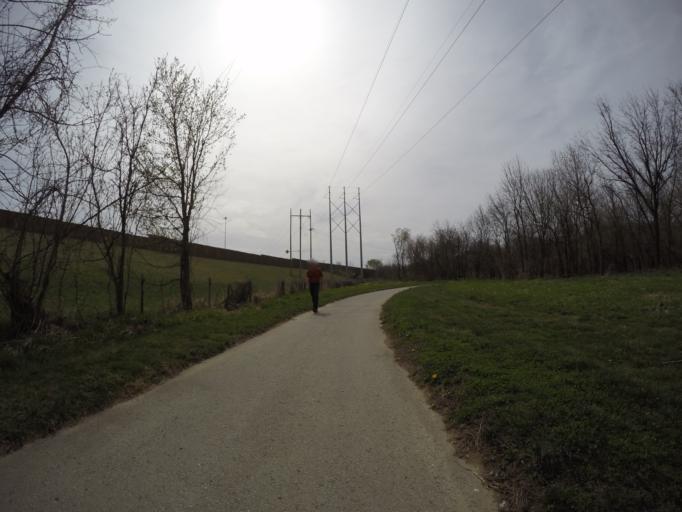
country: US
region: Kansas
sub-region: Johnson County
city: Leawood
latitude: 38.9370
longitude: -94.6105
